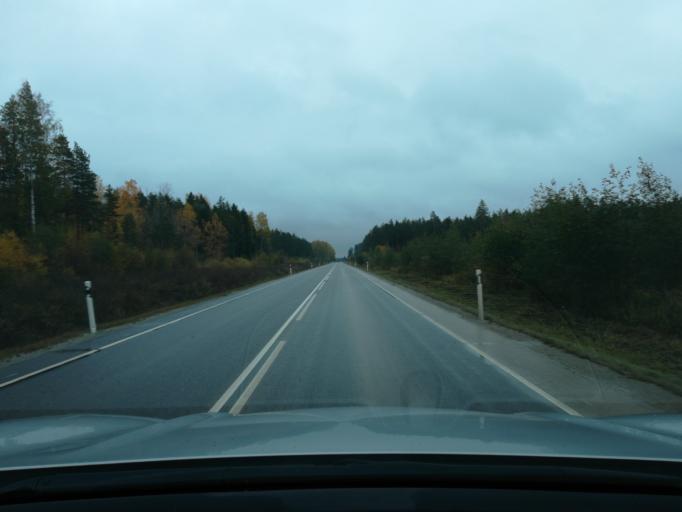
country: EE
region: Ida-Virumaa
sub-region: Johvi vald
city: Johvi
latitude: 59.2999
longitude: 27.4725
